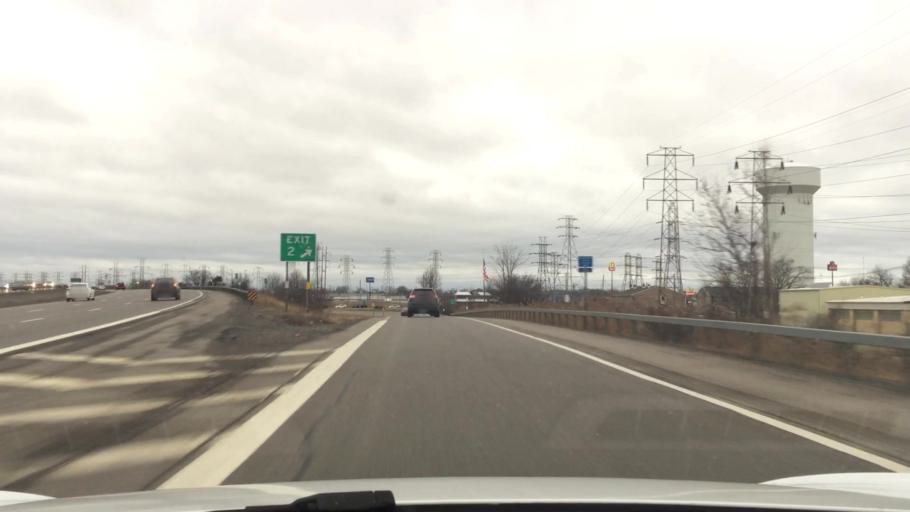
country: US
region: New York
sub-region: Erie County
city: Tonawanda
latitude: 43.0011
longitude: -78.8495
